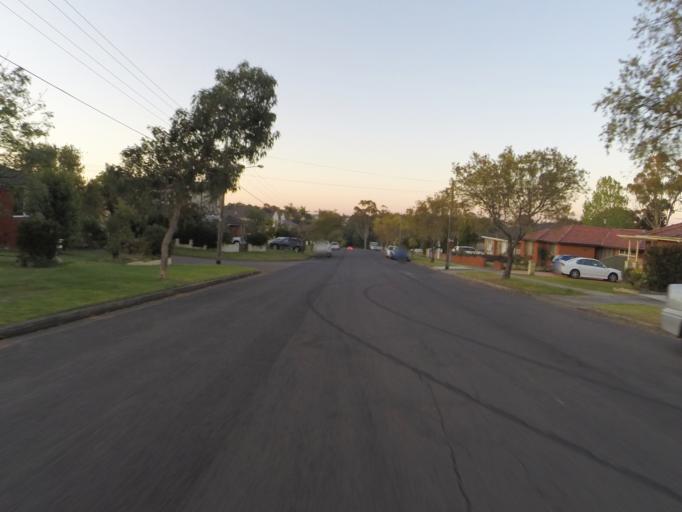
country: AU
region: New South Wales
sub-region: Bankstown
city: Revesby
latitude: -33.9672
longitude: 151.0124
